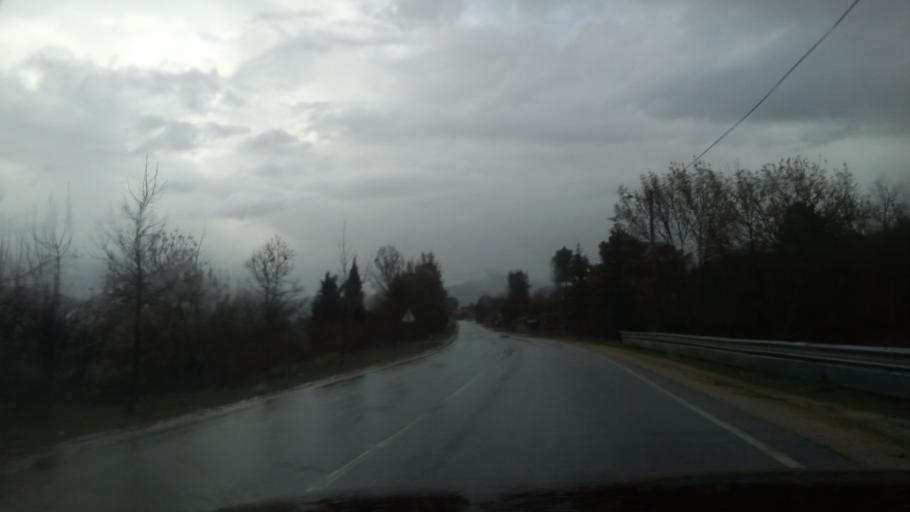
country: PT
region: Guarda
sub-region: Guarda
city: Guarda
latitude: 40.5936
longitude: -7.2895
